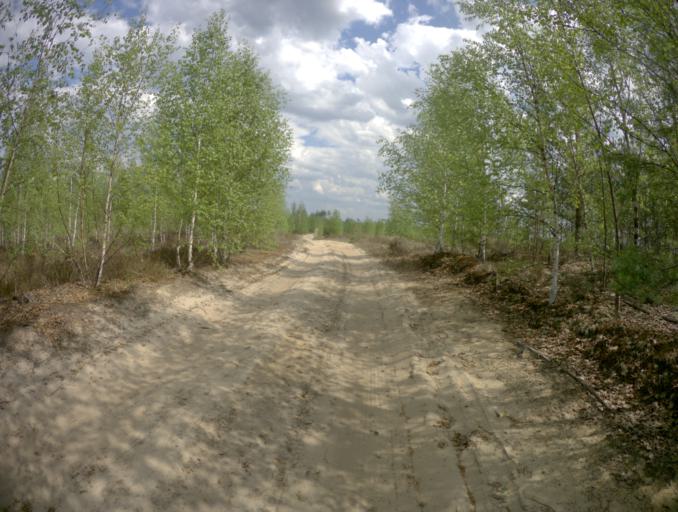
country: RU
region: Ivanovo
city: Talitsy
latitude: 56.4658
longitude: 42.2111
